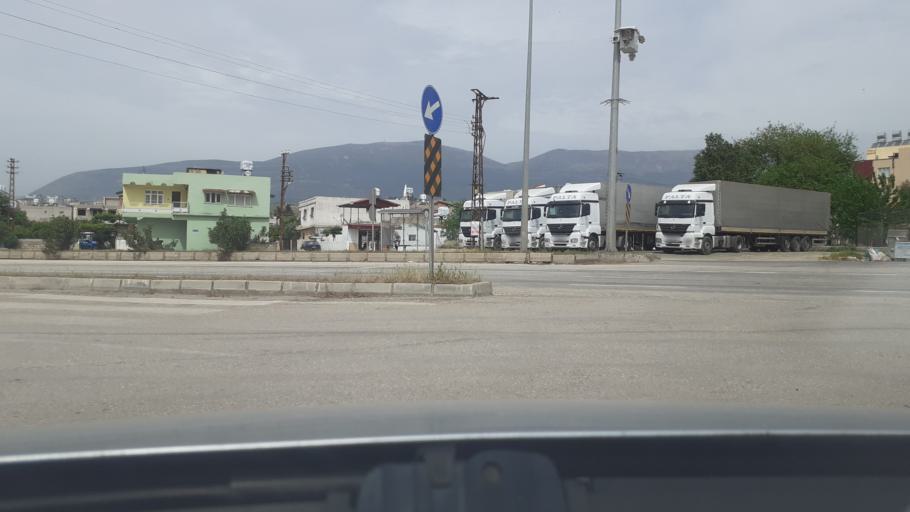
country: TR
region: Hatay
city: Kirikhan
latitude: 36.4836
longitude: 36.3616
